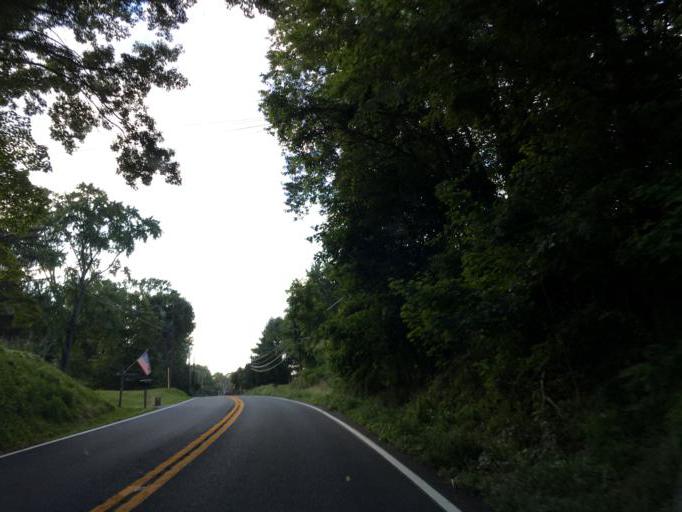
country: US
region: Maryland
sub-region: Harford County
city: Fallston
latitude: 39.5011
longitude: -76.4740
